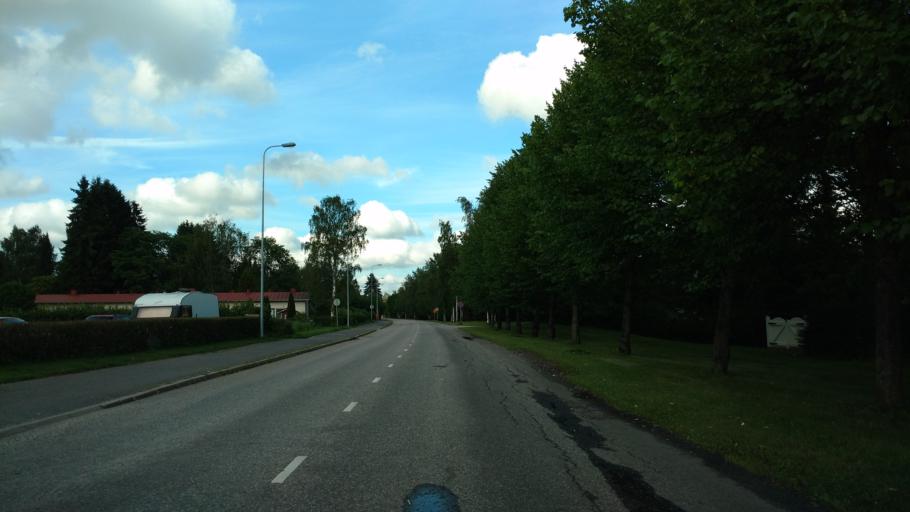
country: FI
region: Varsinais-Suomi
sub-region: Salo
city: Salo
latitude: 60.3973
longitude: 23.1420
